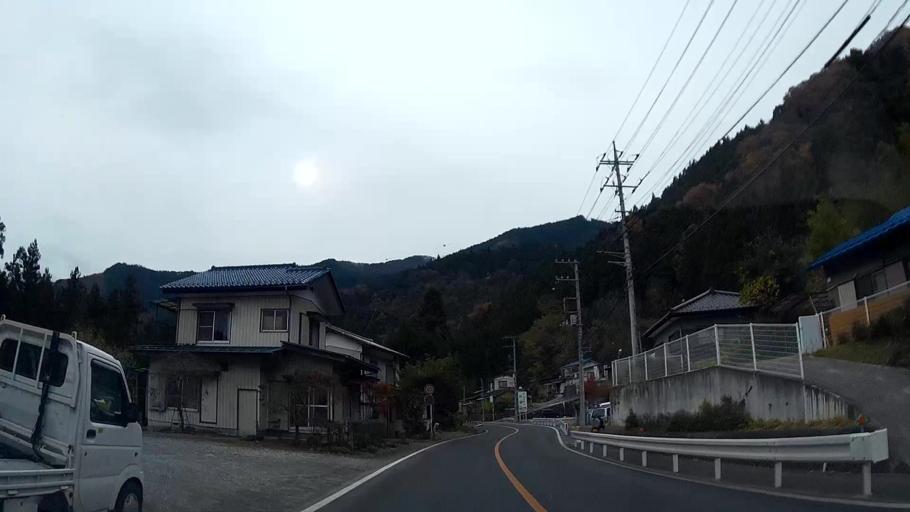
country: JP
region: Saitama
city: Chichibu
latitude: 35.9580
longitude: 138.9659
